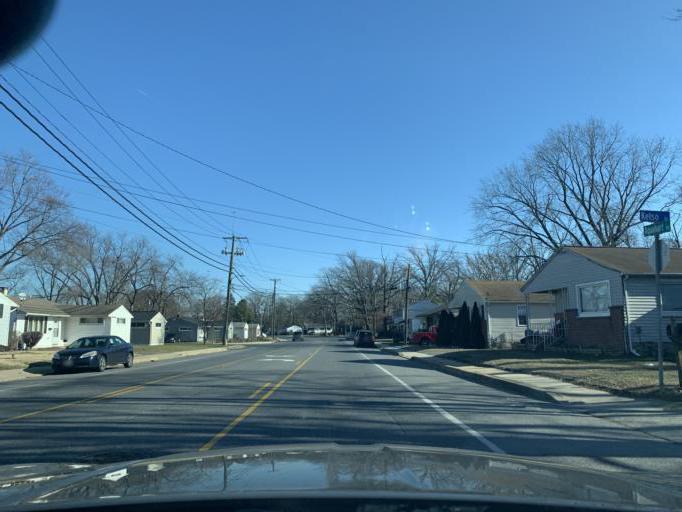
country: US
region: Maryland
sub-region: Anne Arundel County
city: Glen Burnie
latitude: 39.1518
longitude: -76.6286
